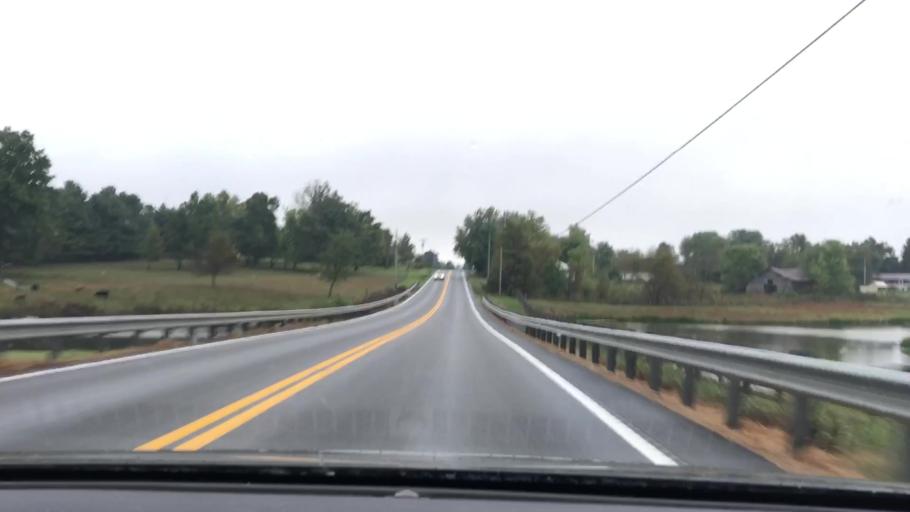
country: US
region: Tennessee
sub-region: Fentress County
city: Grimsley
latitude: 36.1702
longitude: -85.0586
